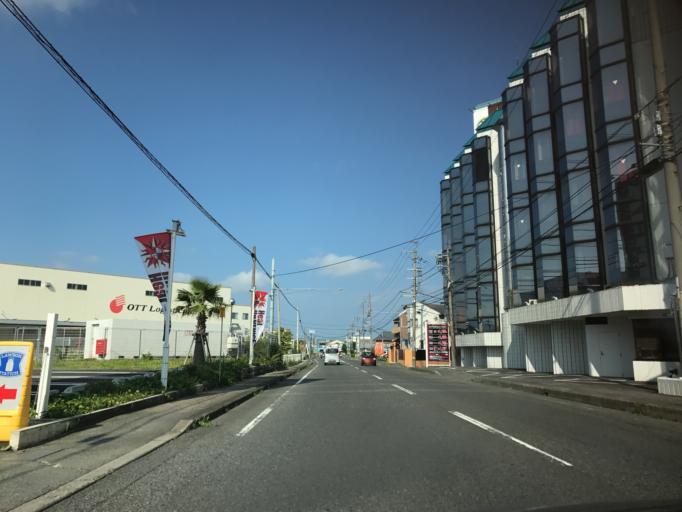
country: JP
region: Shiga Prefecture
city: Kusatsu
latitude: 35.0300
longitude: 136.0067
